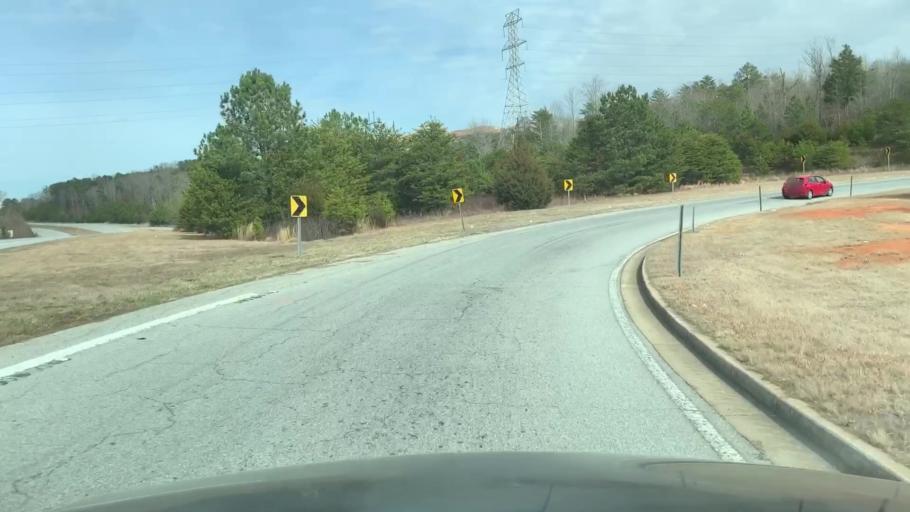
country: US
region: South Carolina
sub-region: Greenville County
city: Golden Grove
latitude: 34.7640
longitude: -82.4505
